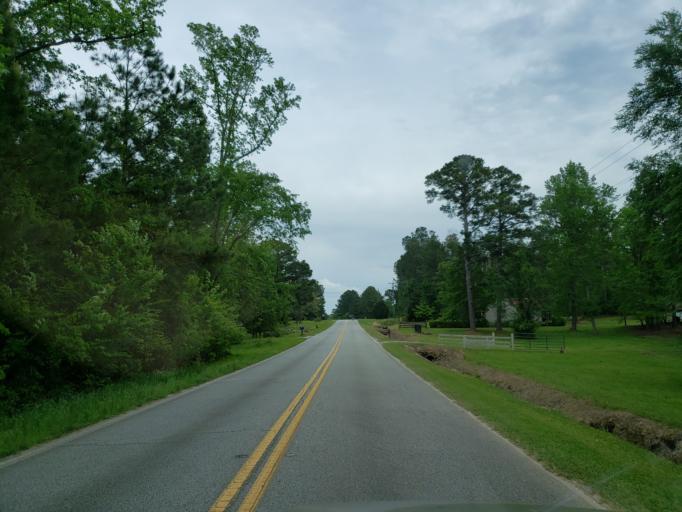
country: US
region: Georgia
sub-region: Bibb County
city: West Point
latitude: 32.8224
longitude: -83.8698
